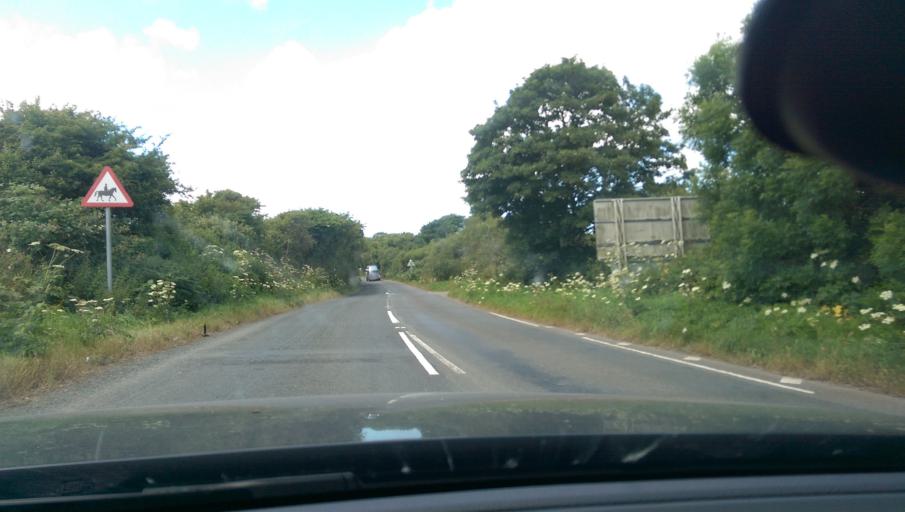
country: GB
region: England
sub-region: Cornwall
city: St. Buryan
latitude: 50.0965
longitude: -5.5955
